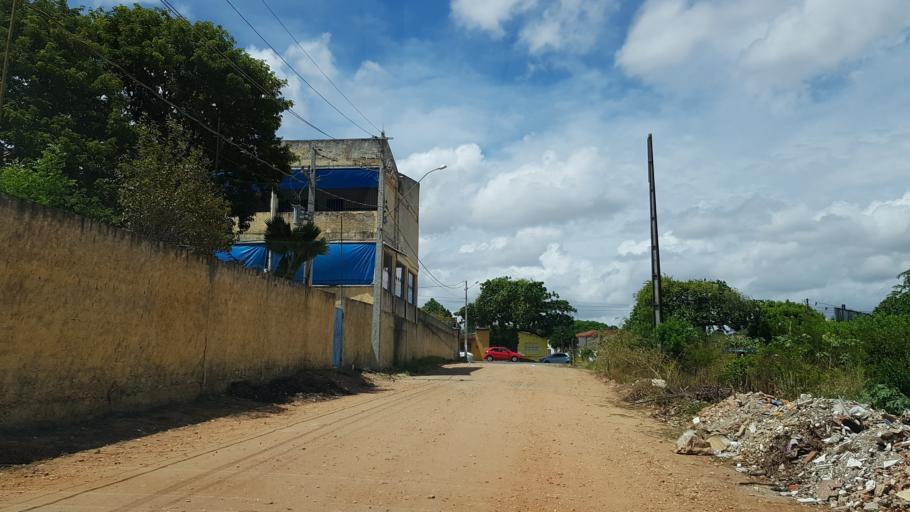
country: BR
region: Alagoas
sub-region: Penedo
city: Penedo
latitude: -10.2841
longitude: -36.5703
